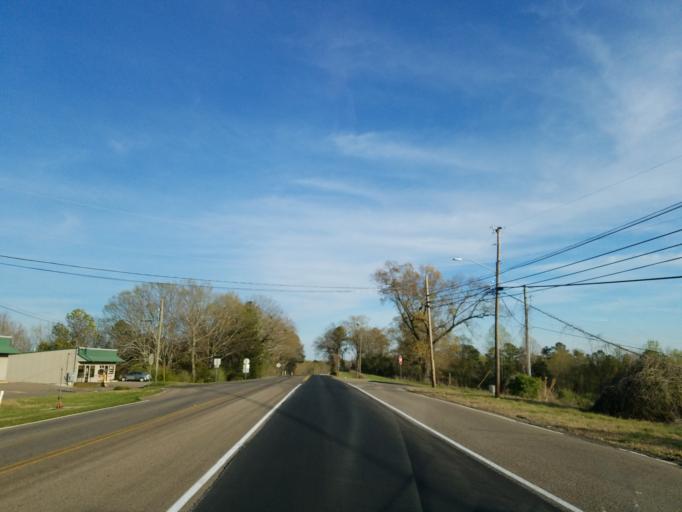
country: US
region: Georgia
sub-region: Pickens County
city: Jasper
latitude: 34.4549
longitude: -84.4083
